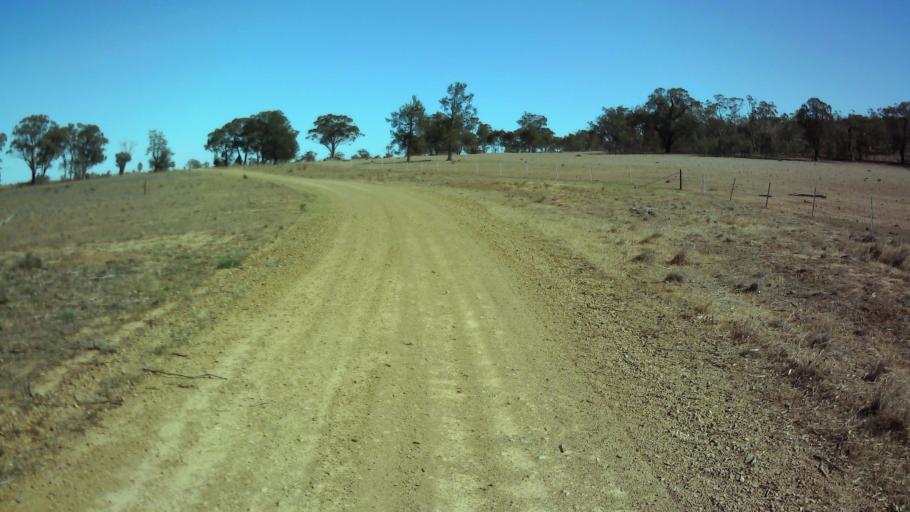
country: AU
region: New South Wales
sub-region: Weddin
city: Grenfell
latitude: -33.7598
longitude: 147.9215
